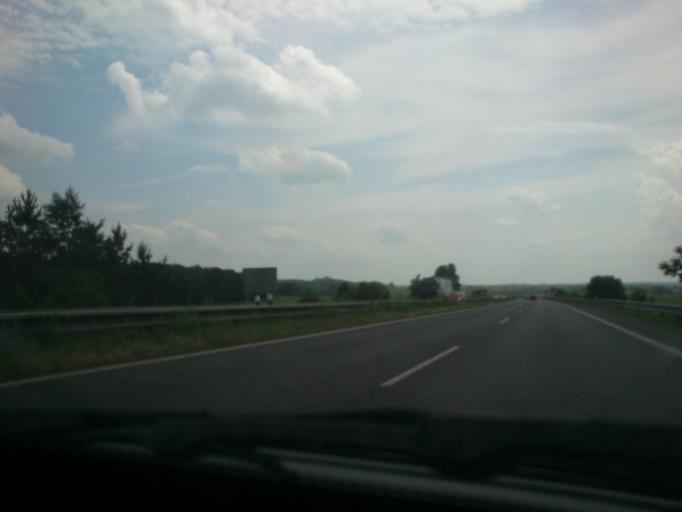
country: CZ
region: Central Bohemia
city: Benatky nad Jizerou
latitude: 50.3098
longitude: 14.8598
